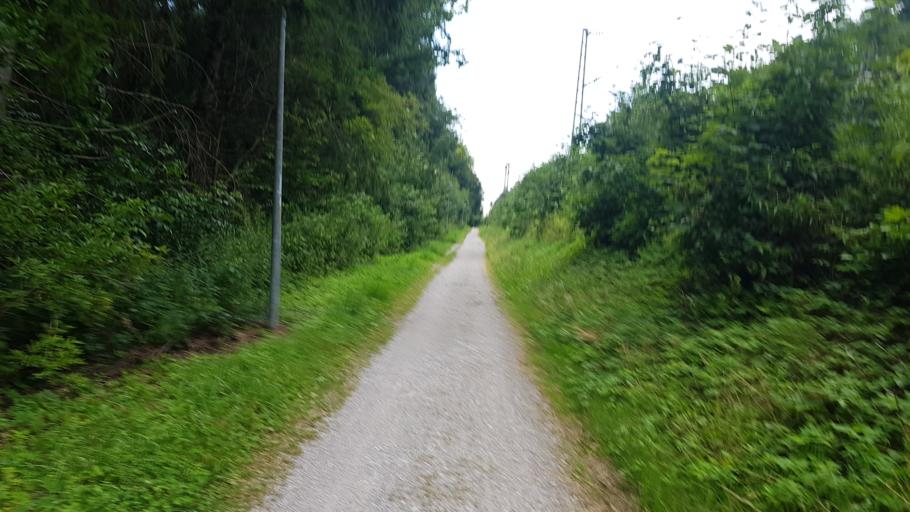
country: DE
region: Bavaria
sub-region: Upper Bavaria
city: Grafrath
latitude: 48.1349
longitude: 11.1601
